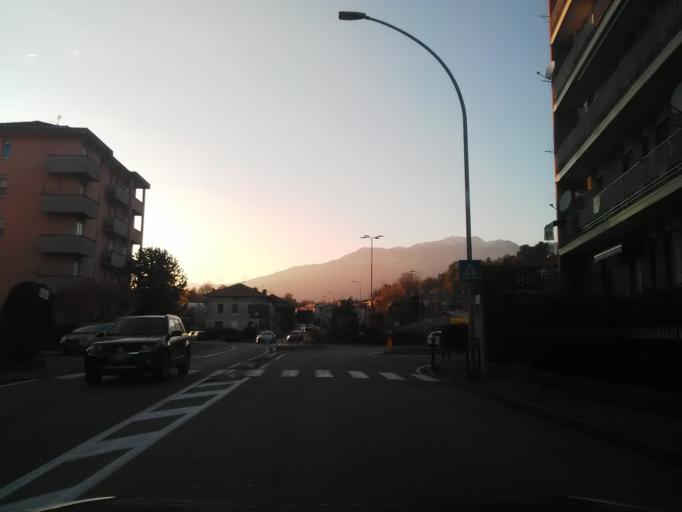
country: IT
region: Piedmont
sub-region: Provincia di Biella
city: Biella
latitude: 45.5571
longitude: 8.0394
